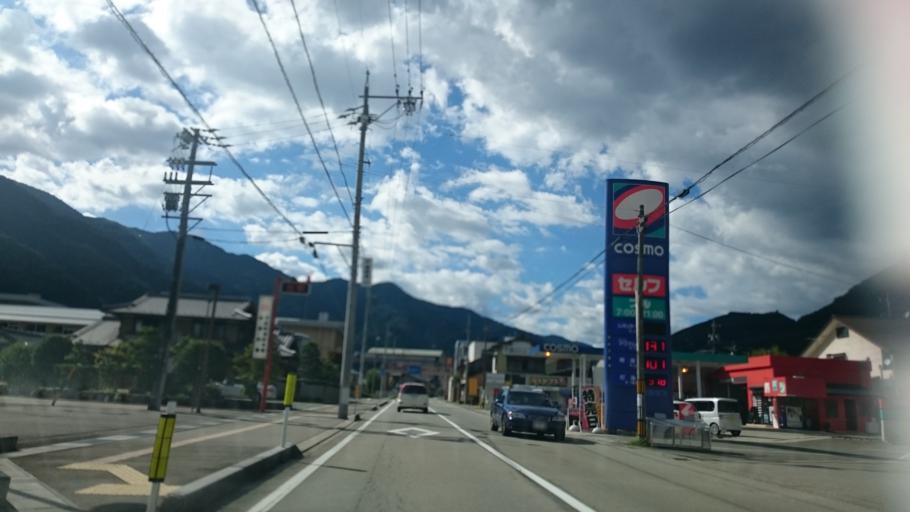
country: JP
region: Gifu
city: Gujo
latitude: 35.8007
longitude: 137.2493
